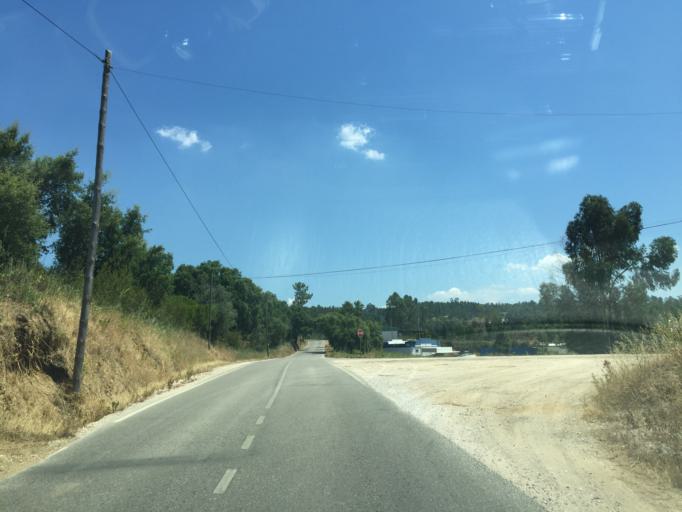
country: PT
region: Santarem
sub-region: Tomar
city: Tomar
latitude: 39.5983
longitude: -8.3163
